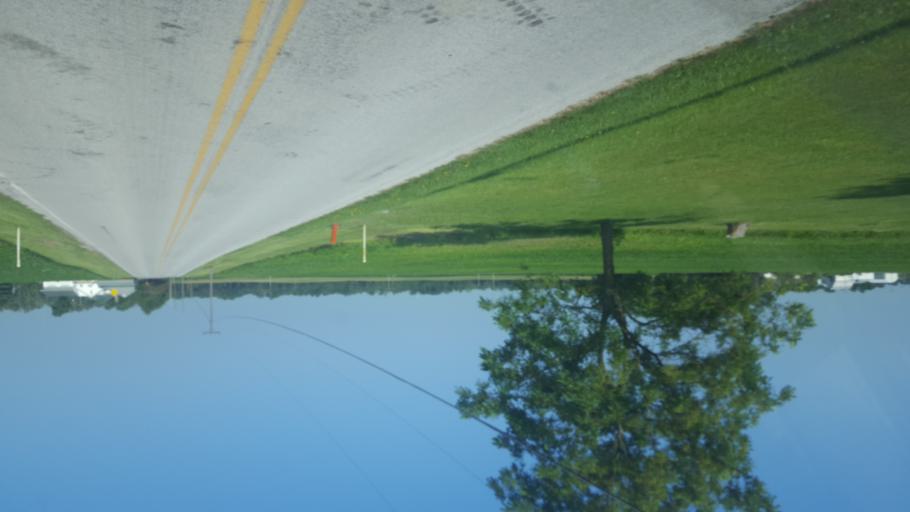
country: US
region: Ohio
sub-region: Hardin County
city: Kenton
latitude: 40.6670
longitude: -83.6067
